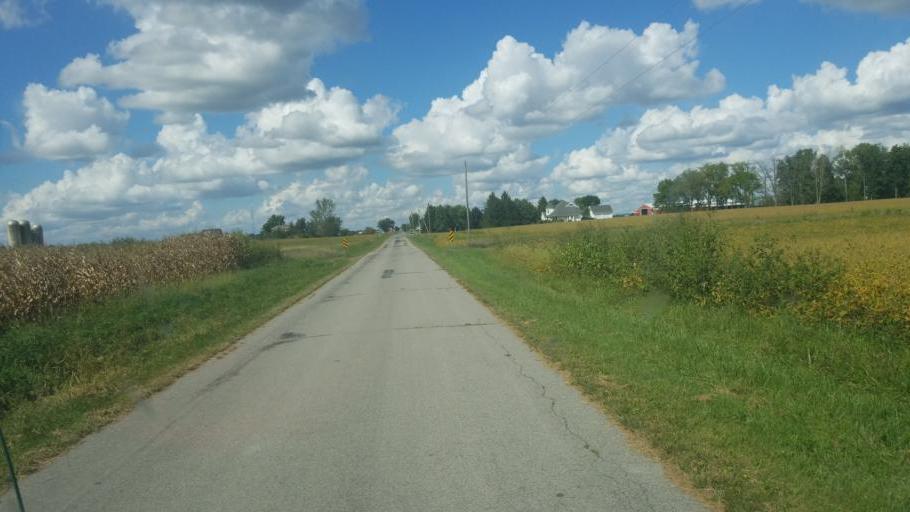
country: US
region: Ohio
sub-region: Hardin County
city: Kenton
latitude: 40.5147
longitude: -83.5400
